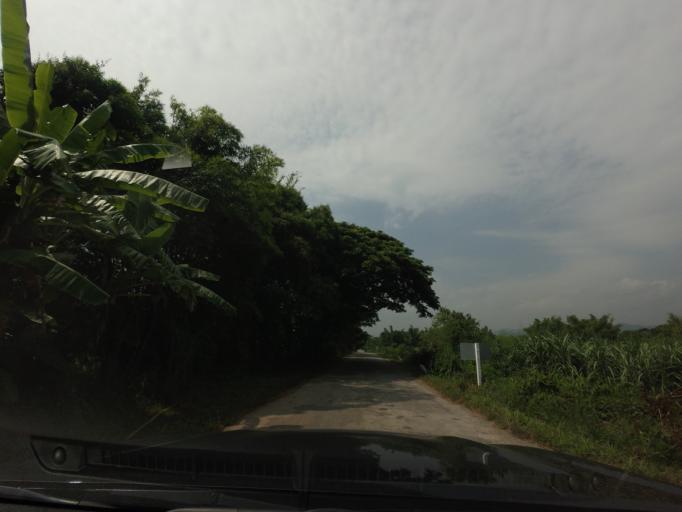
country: LA
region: Xiagnabouli
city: Muang Kenthao
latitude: 17.6736
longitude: 101.3608
